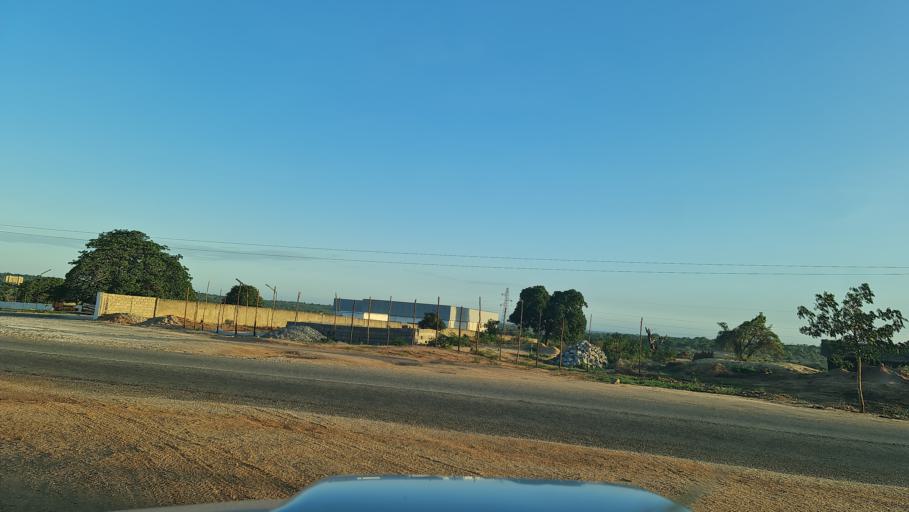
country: MZ
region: Nampula
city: Ilha de Mocambique
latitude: -14.8948
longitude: 40.3129
